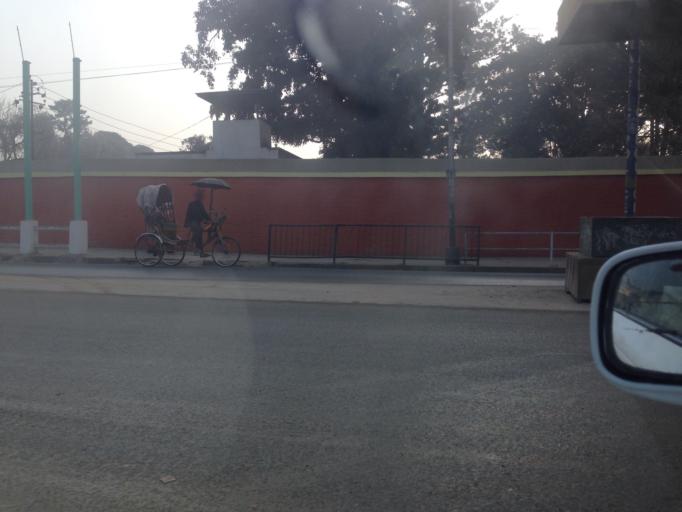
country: NP
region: Central Region
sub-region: Bagmati Zone
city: Kathmandu
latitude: 27.7170
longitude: 85.3159
